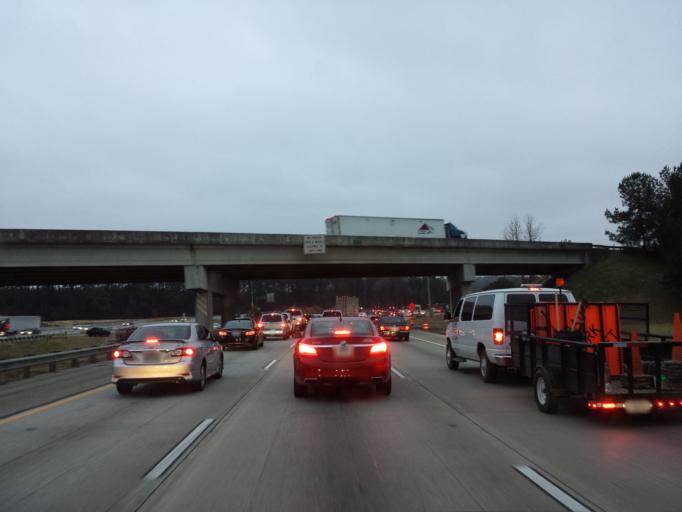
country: US
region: Georgia
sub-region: Henry County
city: Stockbridge
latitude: 33.5437
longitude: -84.2710
